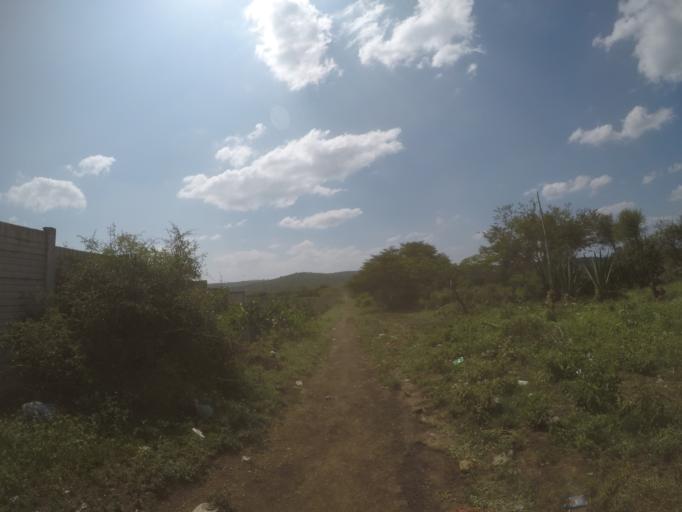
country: ZA
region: KwaZulu-Natal
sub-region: uThungulu District Municipality
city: Empangeni
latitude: -28.5876
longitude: 31.7425
